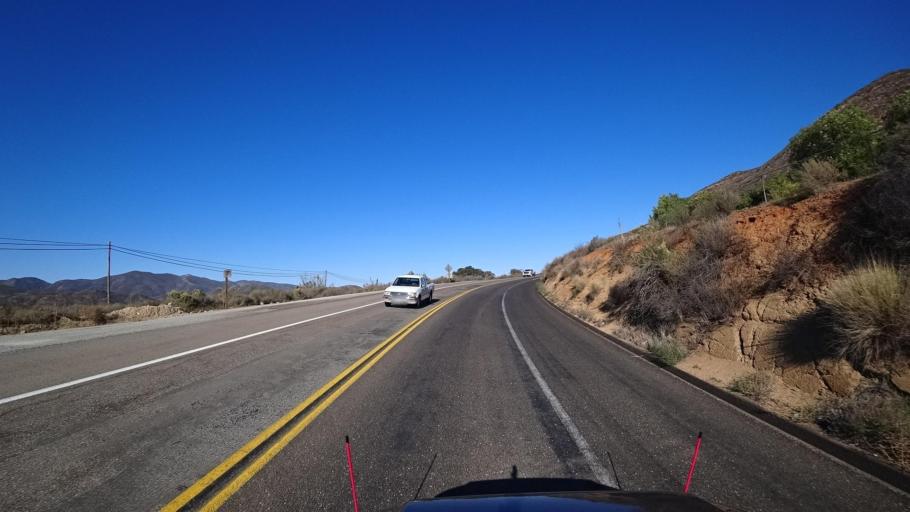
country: MX
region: Baja California
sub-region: Tijuana
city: Villa del Campo
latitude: 32.6166
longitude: -116.7377
